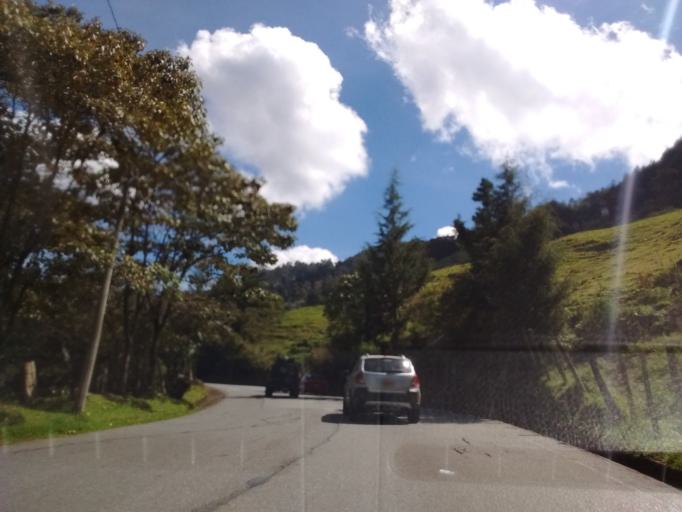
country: CO
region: Antioquia
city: Medellin
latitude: 6.2369
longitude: -75.5134
